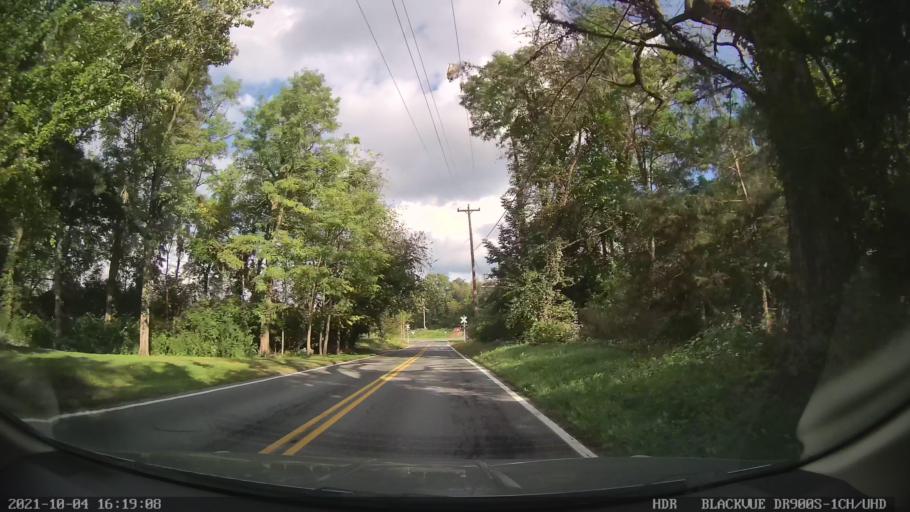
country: US
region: Pennsylvania
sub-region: Berks County
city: Blandon
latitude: 40.4343
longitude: -75.8985
